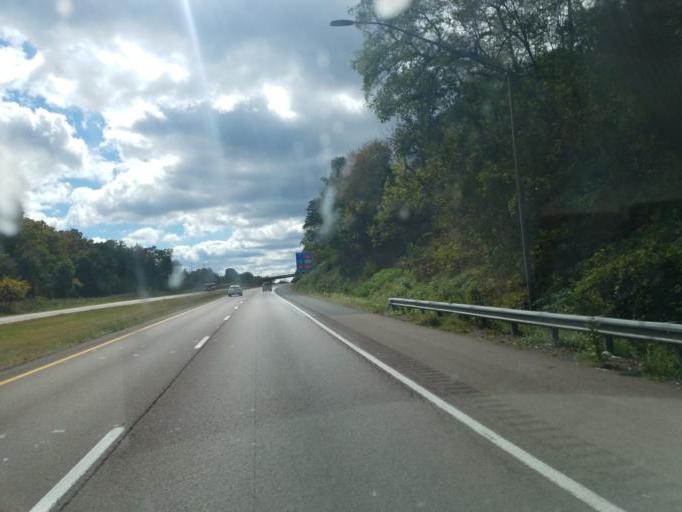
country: US
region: Maryland
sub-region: Allegany County
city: Cumberland
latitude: 39.6699
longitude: -78.7339
